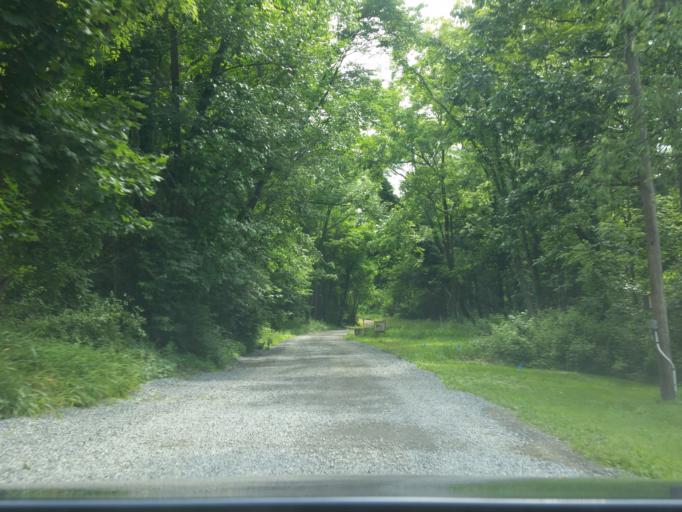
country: US
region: Pennsylvania
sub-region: Lebanon County
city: Jonestown
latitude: 40.4374
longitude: -76.5280
